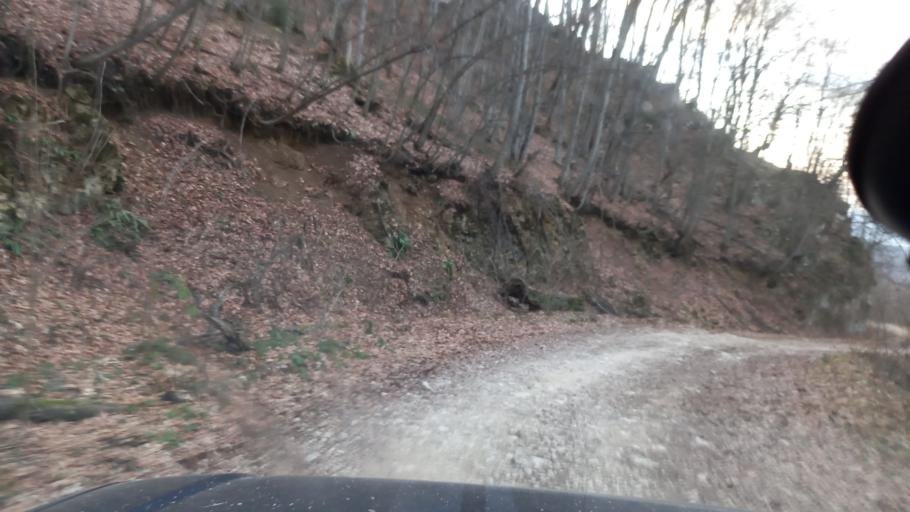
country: RU
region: Krasnodarskiy
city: Neftegorsk
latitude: 44.2199
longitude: 39.9036
